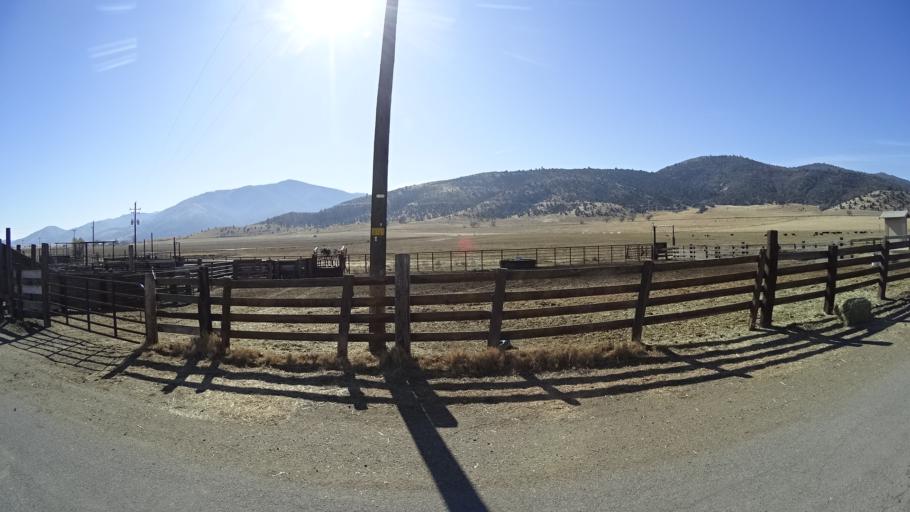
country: US
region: California
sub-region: Siskiyou County
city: Weed
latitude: 41.5269
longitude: -122.5315
